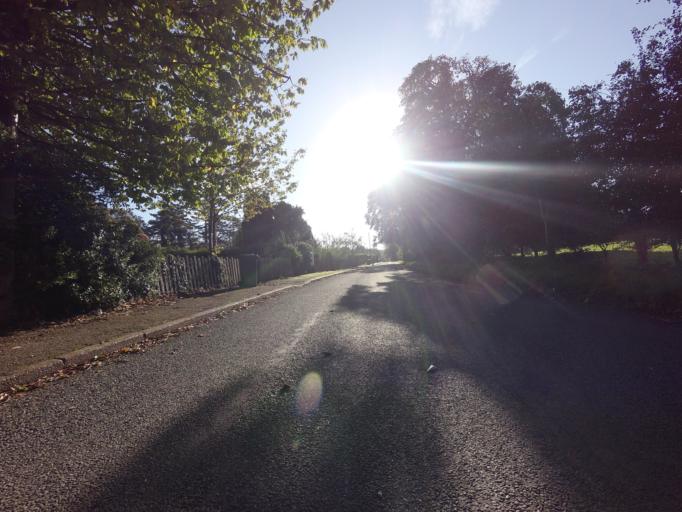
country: GB
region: England
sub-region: Norfolk
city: Dersingham
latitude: 52.8359
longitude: 0.5816
